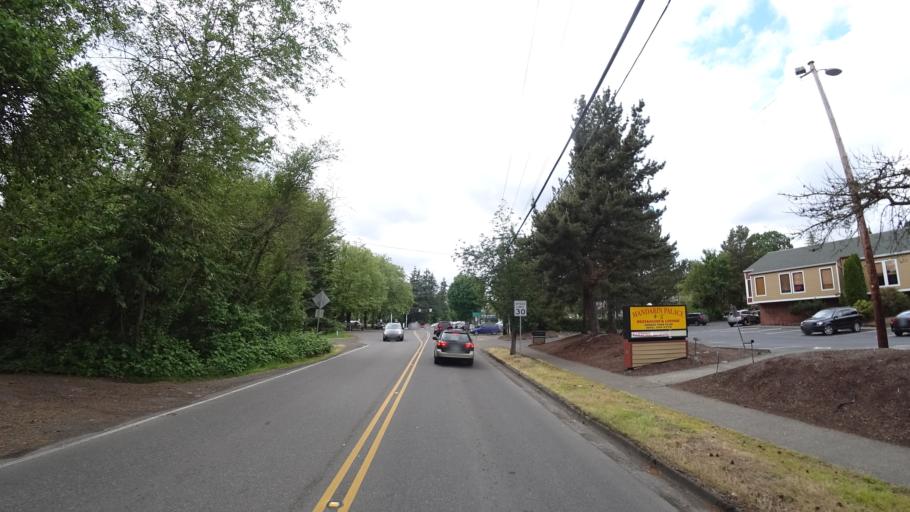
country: US
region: Oregon
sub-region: Washington County
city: Raleigh Hills
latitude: 45.4716
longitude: -122.7722
